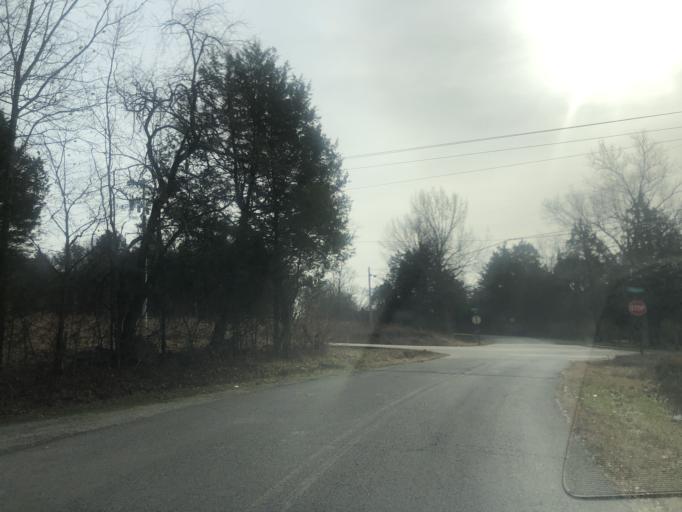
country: US
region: Tennessee
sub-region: Williamson County
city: Nolensville
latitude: 35.8625
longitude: -86.5783
